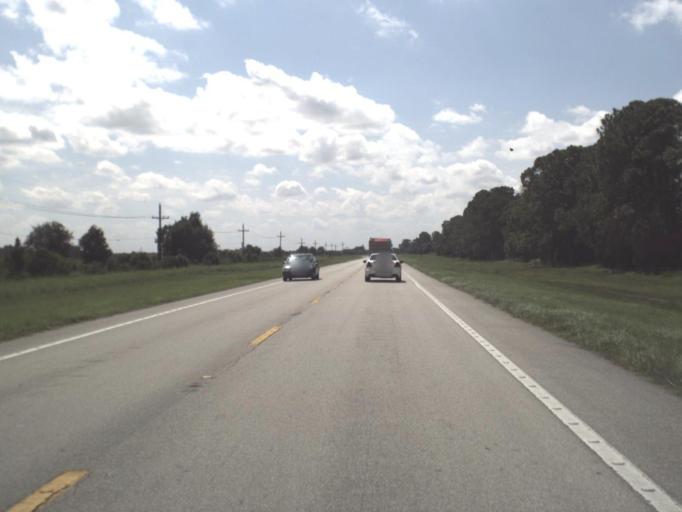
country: US
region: Florida
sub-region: Hendry County
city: Port LaBelle
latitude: 26.6032
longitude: -81.4367
